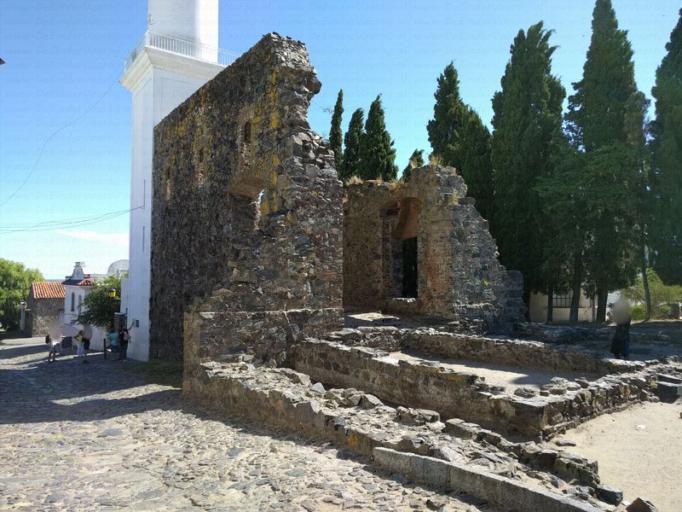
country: UY
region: Colonia
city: Colonia del Sacramento
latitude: -34.4726
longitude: -57.8522
